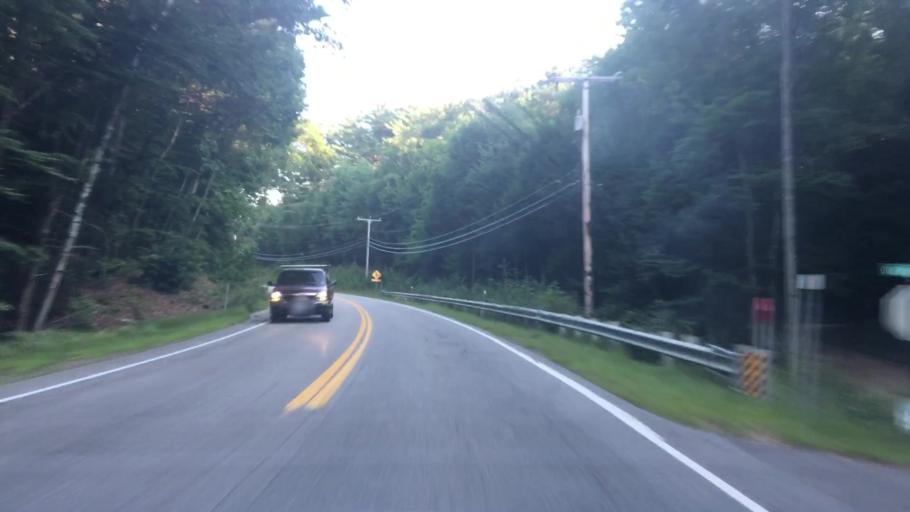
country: US
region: New Hampshire
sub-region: Belknap County
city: Laconia
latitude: 43.4973
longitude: -71.4460
